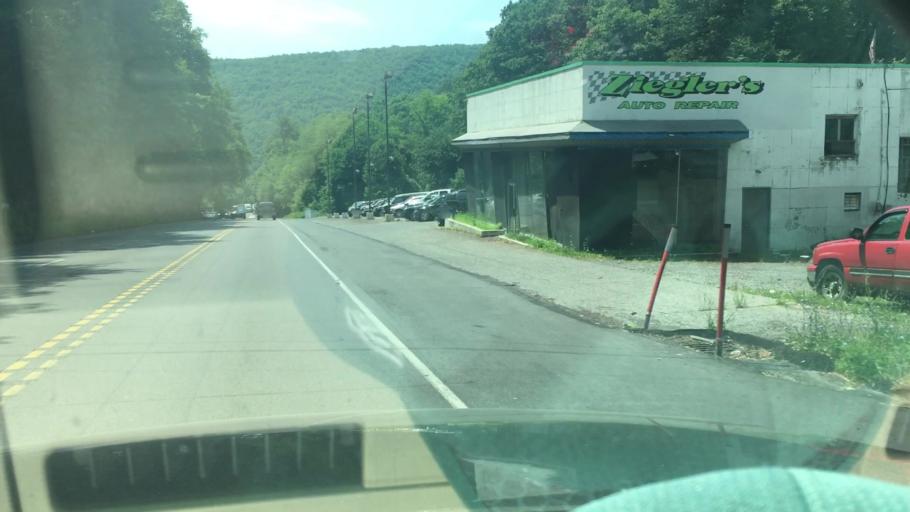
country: US
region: Pennsylvania
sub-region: Schuylkill County
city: Hometown
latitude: 40.8195
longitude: -75.9788
